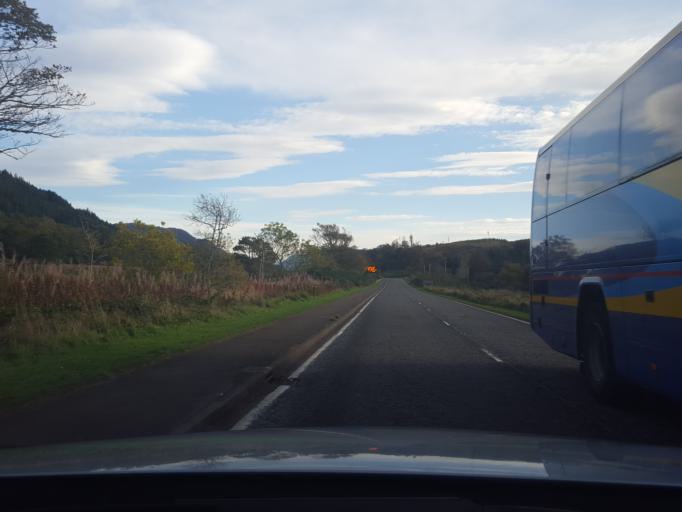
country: GB
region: Scotland
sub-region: Highland
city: Portree
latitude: 57.2824
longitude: -5.6246
